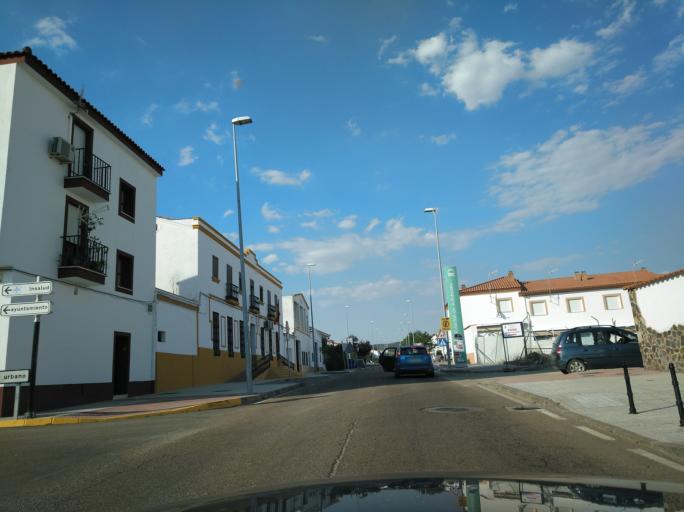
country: ES
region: Extremadura
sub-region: Provincia de Badajoz
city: Alconchel
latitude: 38.5156
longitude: -7.0686
